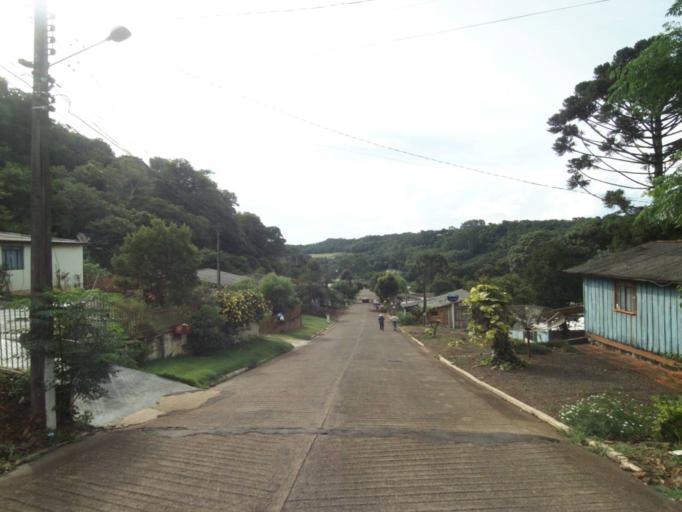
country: BR
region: Parana
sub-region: Guaraniacu
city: Guaraniacu
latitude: -25.1020
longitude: -52.8728
